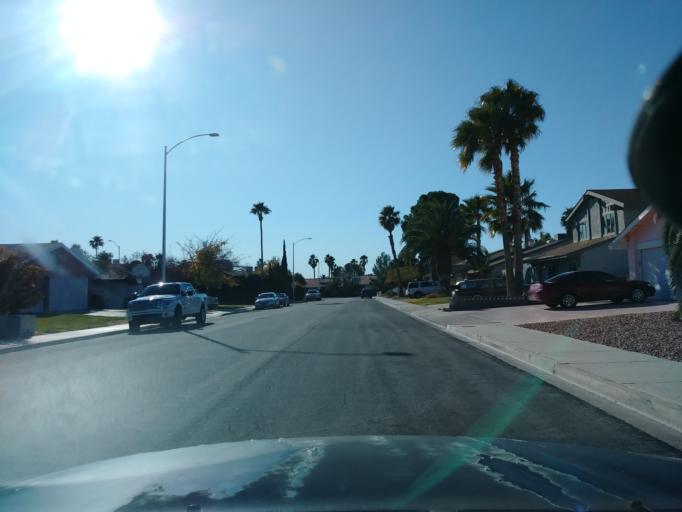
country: US
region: Nevada
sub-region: Clark County
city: Spring Valley
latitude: 36.1493
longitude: -115.2324
